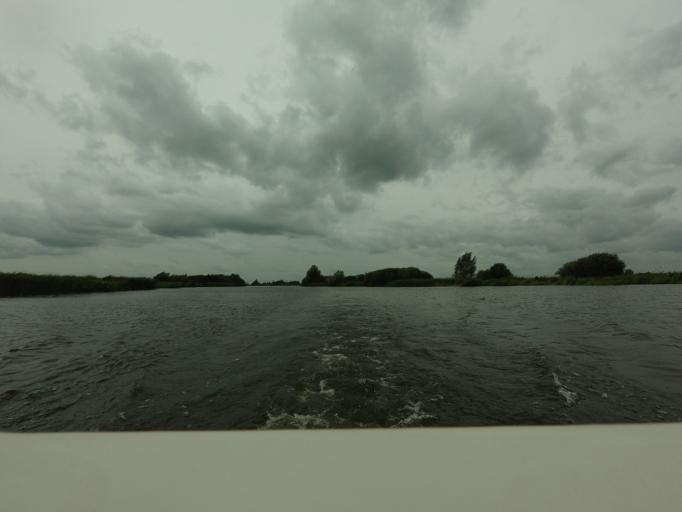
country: NL
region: Friesland
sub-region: Gemeente Boarnsterhim
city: Warten
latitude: 53.1004
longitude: 5.9152
